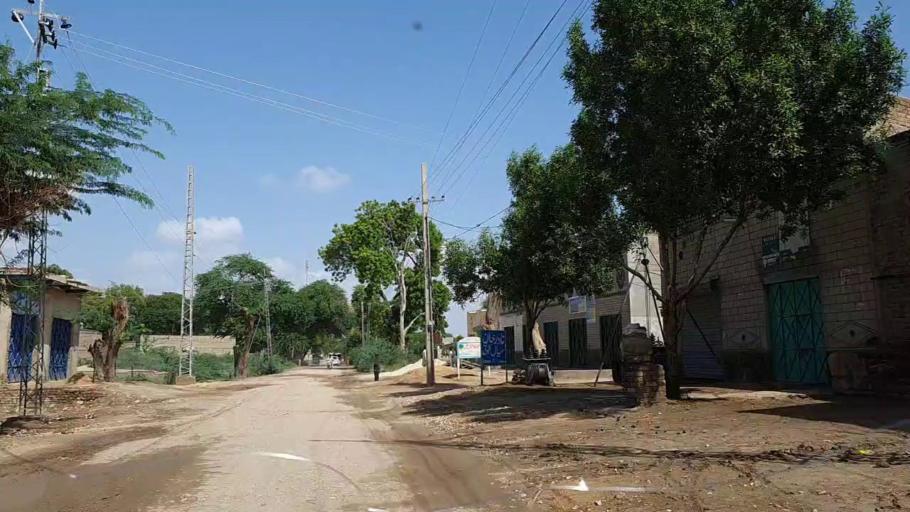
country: PK
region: Sindh
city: Pad Idan
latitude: 26.7768
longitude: 68.2936
